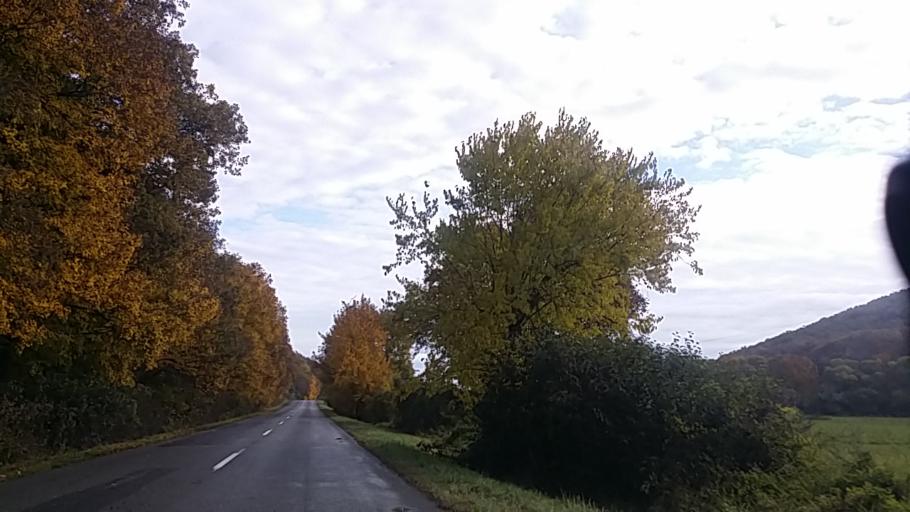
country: HU
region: Heves
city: Szilvasvarad
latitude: 48.1489
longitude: 20.4517
